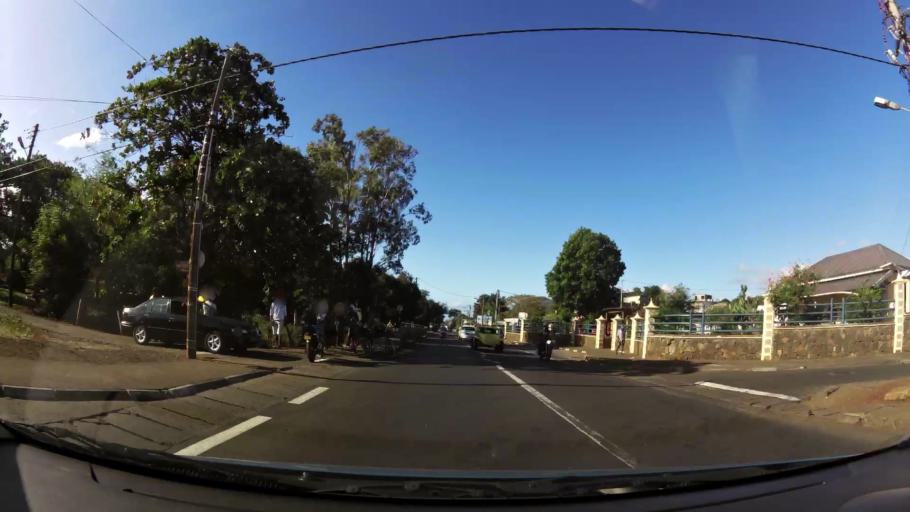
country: MU
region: Black River
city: Petite Riviere
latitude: -20.1864
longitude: 57.4597
